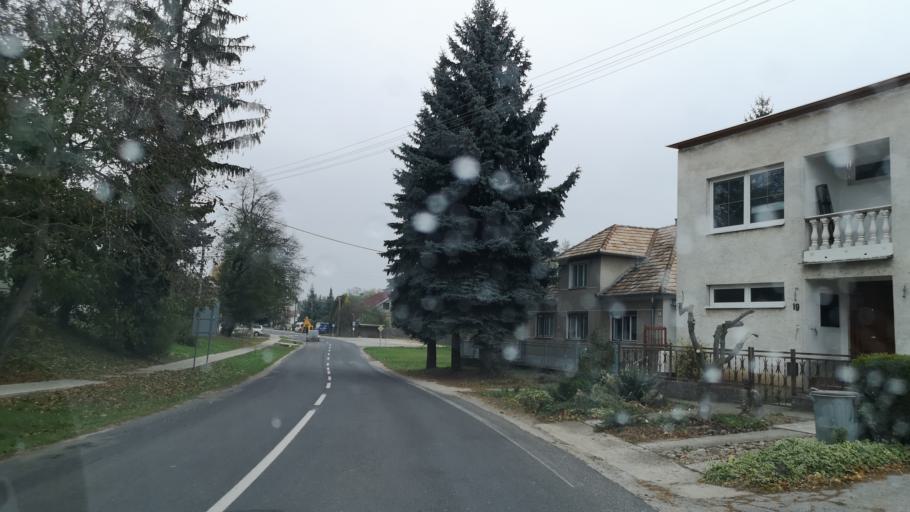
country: SK
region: Trnavsky
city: Vrbove
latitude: 48.5253
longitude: 17.6102
